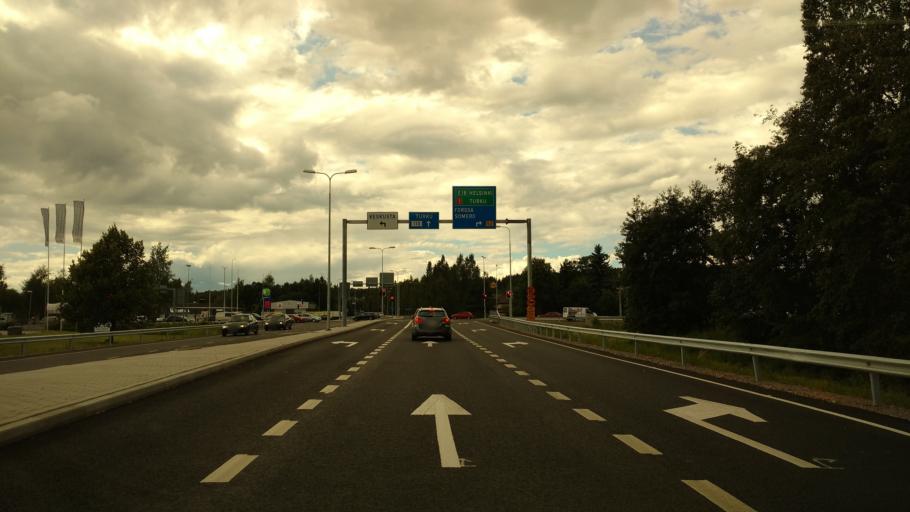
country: FI
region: Varsinais-Suomi
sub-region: Salo
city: Salo
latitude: 60.3931
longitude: 23.1339
